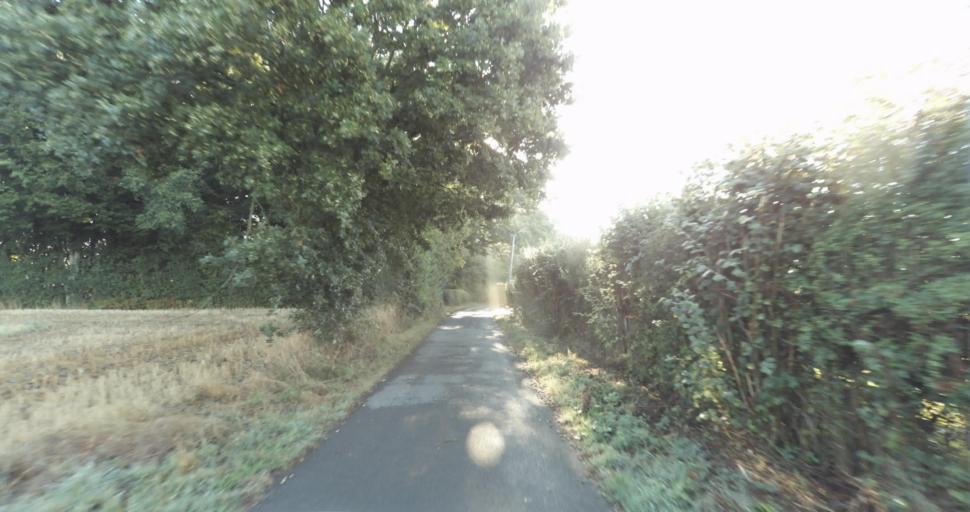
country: FR
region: Lower Normandy
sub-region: Departement de l'Orne
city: Vimoutiers
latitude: 48.9114
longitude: 0.1602
